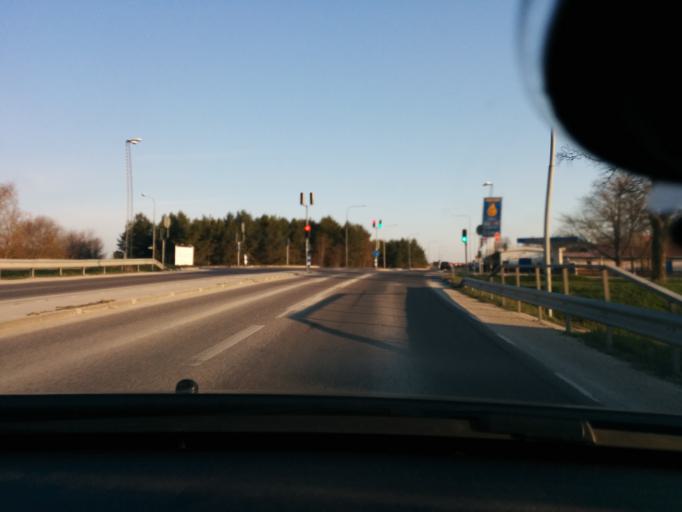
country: SE
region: Gotland
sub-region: Gotland
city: Visby
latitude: 57.6162
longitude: 18.2847
